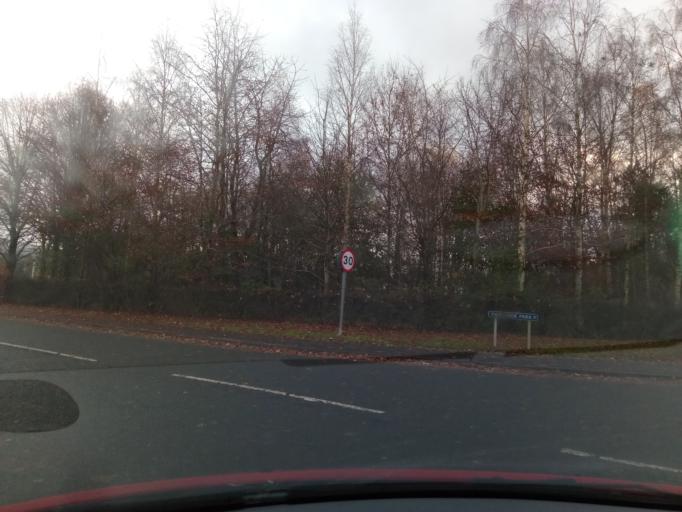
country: GB
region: Scotland
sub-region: The Scottish Borders
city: Melrose
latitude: 55.6033
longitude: -2.7523
